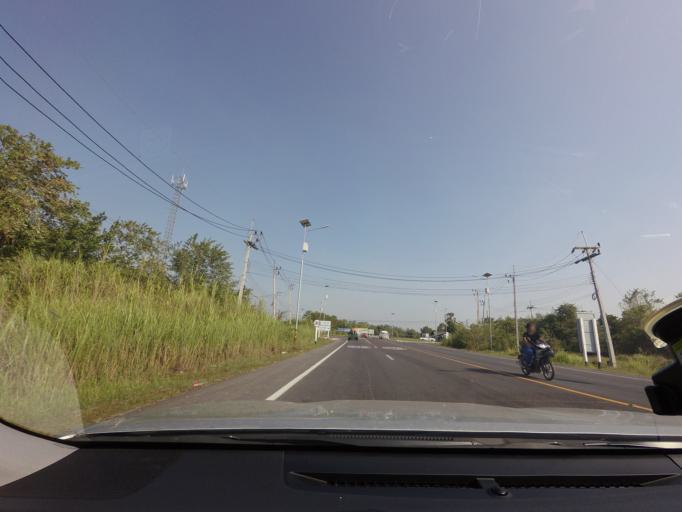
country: TH
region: Nakhon Si Thammarat
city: Nakhon Si Thammarat
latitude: 8.5113
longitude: 99.9690
